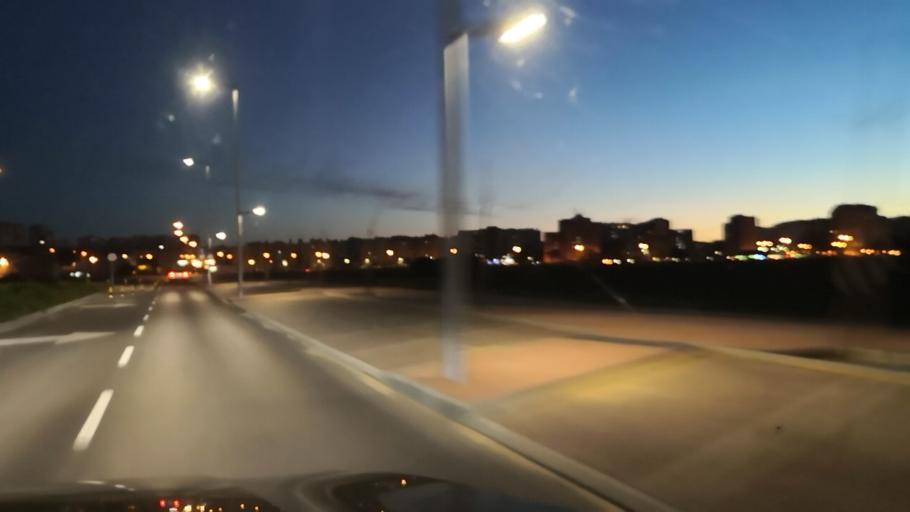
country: PT
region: Setubal
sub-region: Setubal
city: Setubal
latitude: 38.5371
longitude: -8.8859
